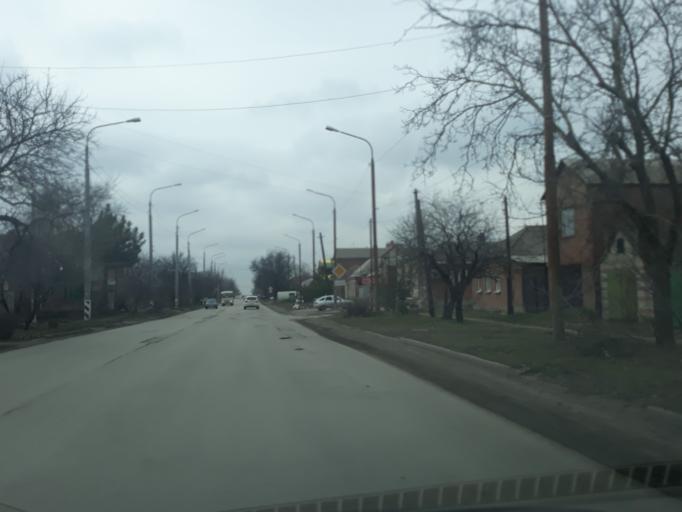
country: RU
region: Rostov
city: Taganrog
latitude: 47.2725
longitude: 38.9062
